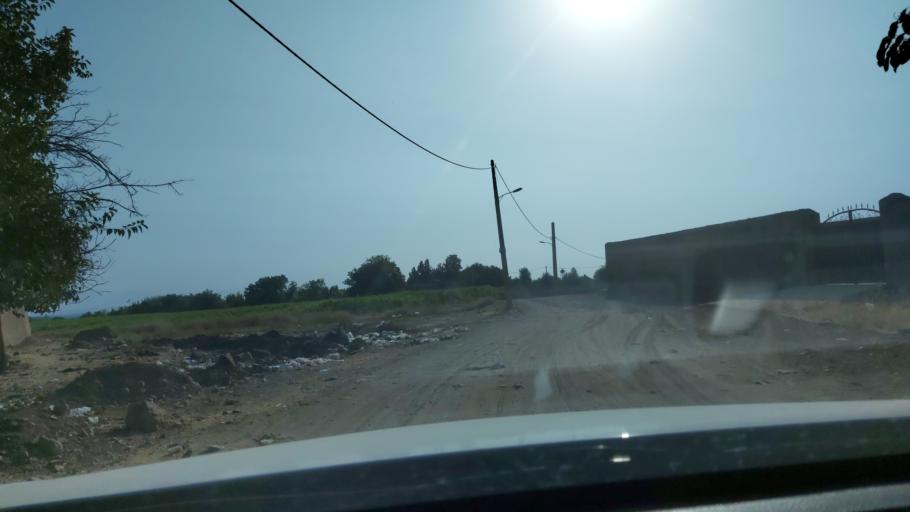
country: IR
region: Alborz
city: Hashtgerd
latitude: 35.9540
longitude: 50.7818
